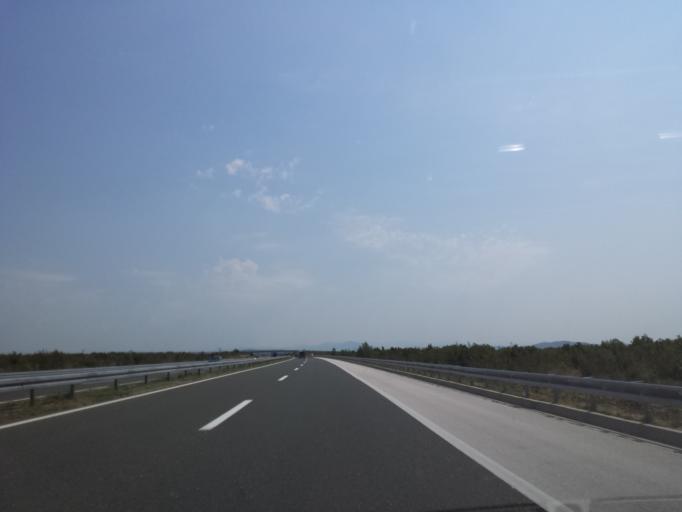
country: HR
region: Sibensko-Kniniska
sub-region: Grad Sibenik
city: Pirovac
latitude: 43.9112
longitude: 15.7518
